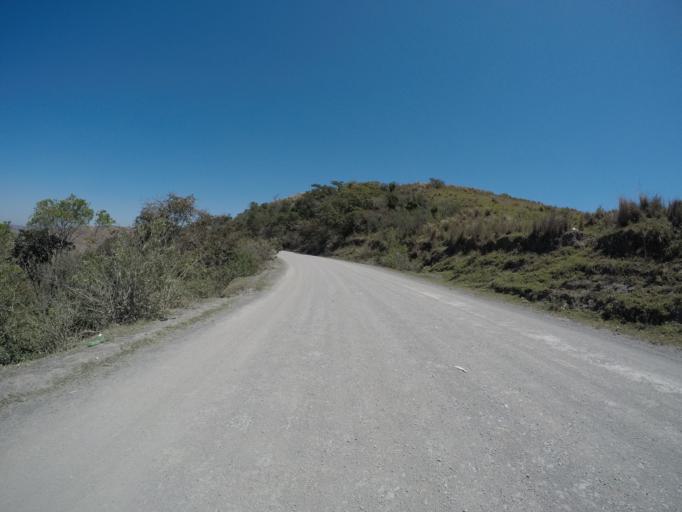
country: ZA
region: Eastern Cape
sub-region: OR Tambo District Municipality
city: Libode
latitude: -31.9974
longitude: 29.0626
